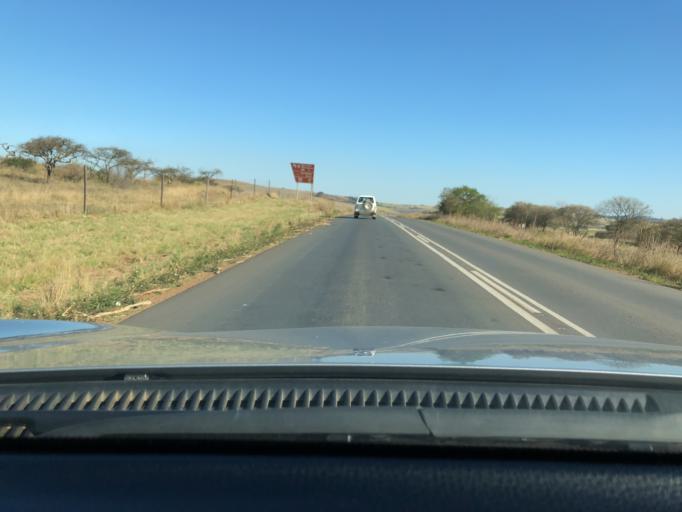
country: ZA
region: KwaZulu-Natal
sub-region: uMgungundlovu District Municipality
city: Camperdown
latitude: -29.8254
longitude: 30.5231
